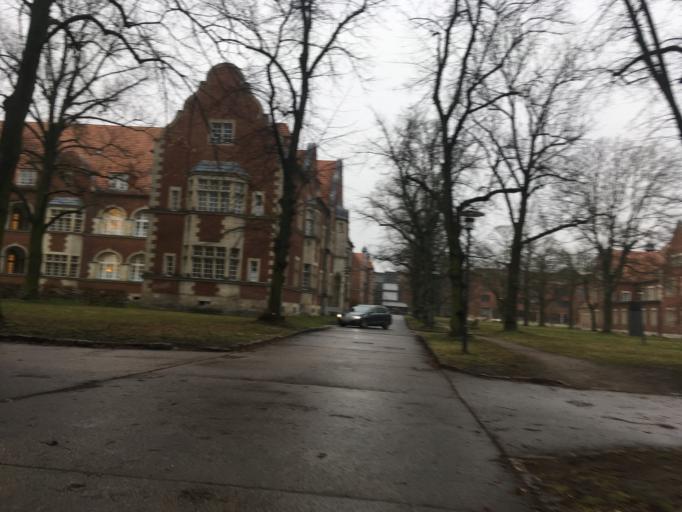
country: DE
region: Berlin
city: Buch
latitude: 52.6323
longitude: 13.5076
